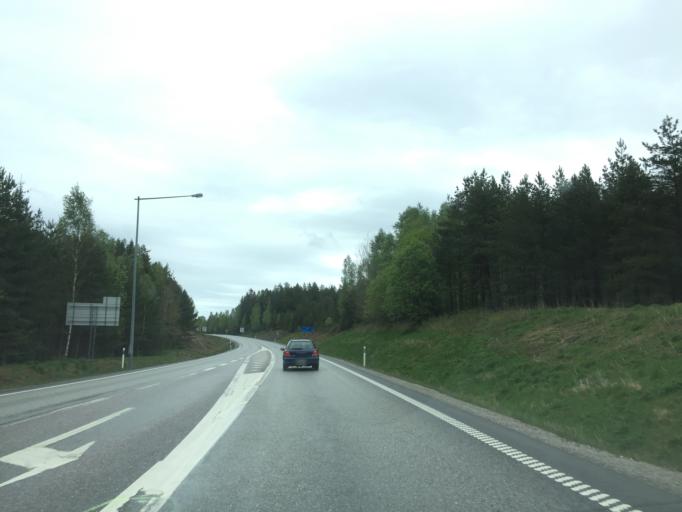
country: SE
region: OErebro
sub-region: Lindesbergs Kommun
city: Lindesberg
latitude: 59.5549
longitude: 15.2208
